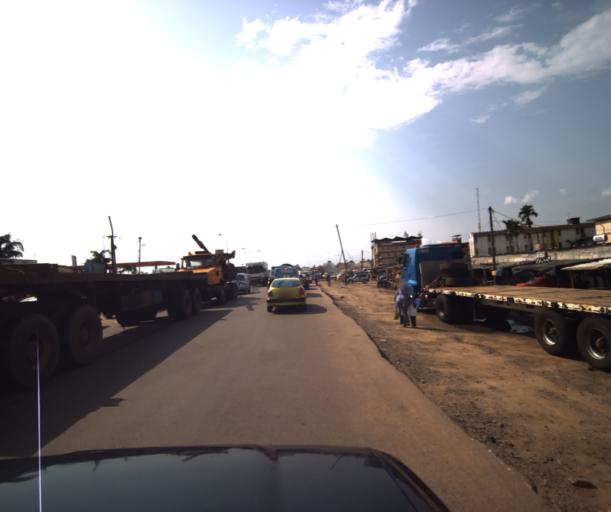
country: CM
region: Littoral
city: Douala
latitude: 4.0152
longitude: 9.7277
